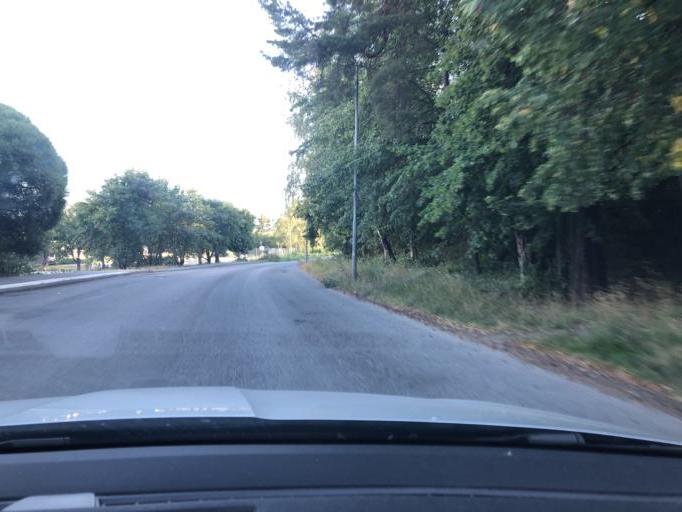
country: SE
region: Stockholm
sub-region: Sodertalje Kommun
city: Soedertaelje
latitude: 59.1791
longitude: 17.6206
